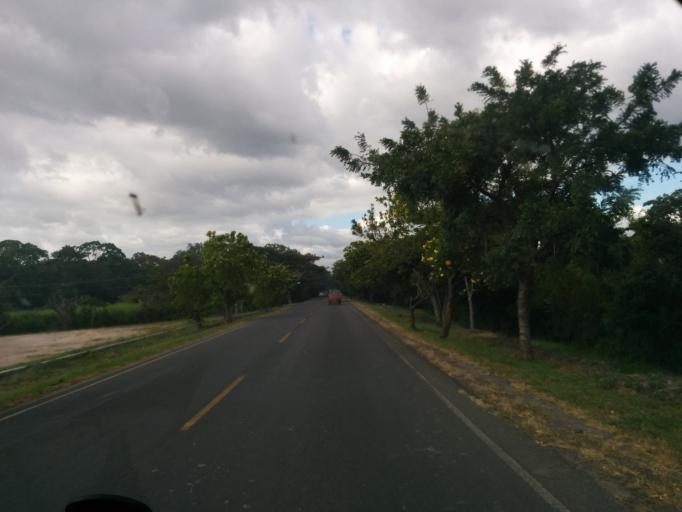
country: NI
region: Esteli
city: Esteli
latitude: 13.1323
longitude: -86.3653
